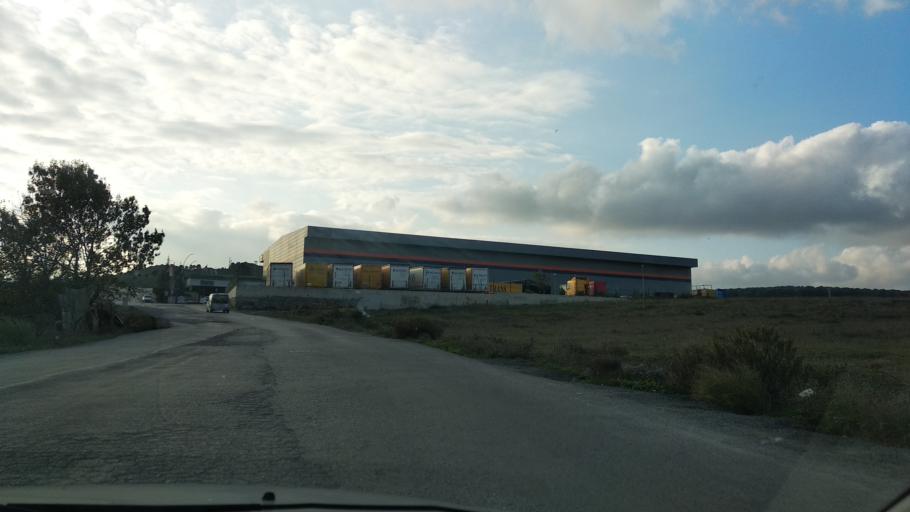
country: TR
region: Istanbul
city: Icmeler
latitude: 40.9203
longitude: 29.3456
